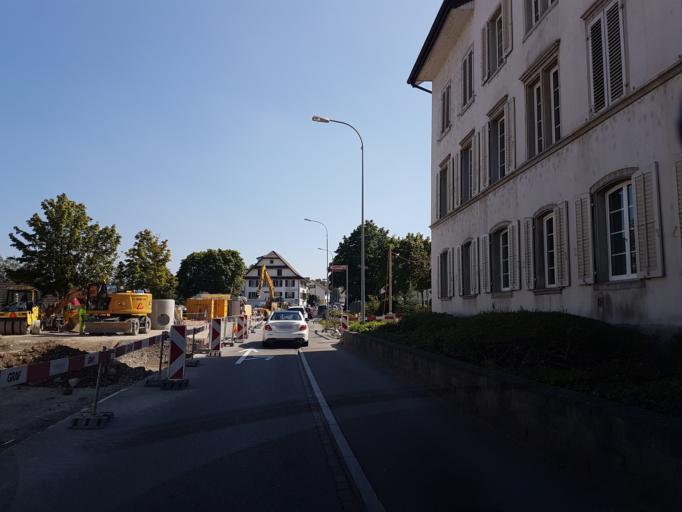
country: CH
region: Aargau
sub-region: Bezirk Muri
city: Waltenschwil
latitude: 47.3029
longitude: 8.3122
